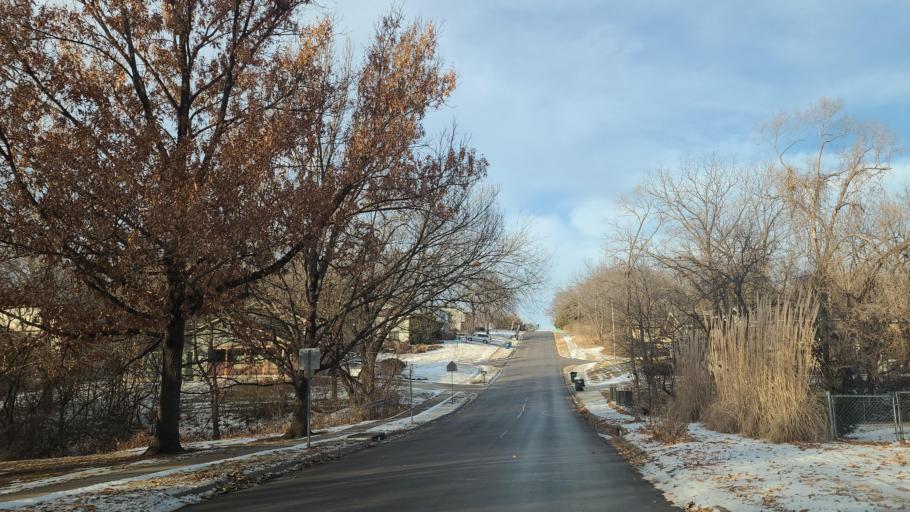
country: US
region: Kansas
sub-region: Douglas County
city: Lawrence
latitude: 38.9643
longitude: -95.2751
